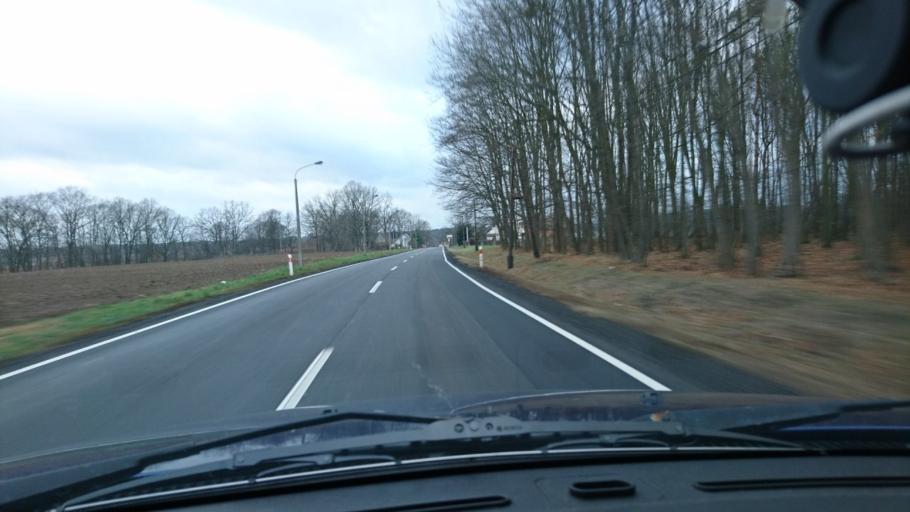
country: PL
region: Opole Voivodeship
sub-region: Powiat oleski
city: Olesno
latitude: 50.9100
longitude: 18.3576
